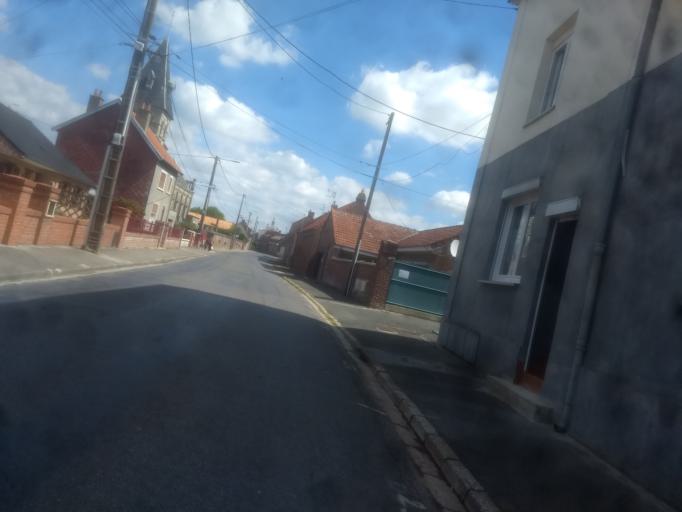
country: FR
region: Nord-Pas-de-Calais
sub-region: Departement du Pas-de-Calais
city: Agny
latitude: 50.2586
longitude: 2.7566
